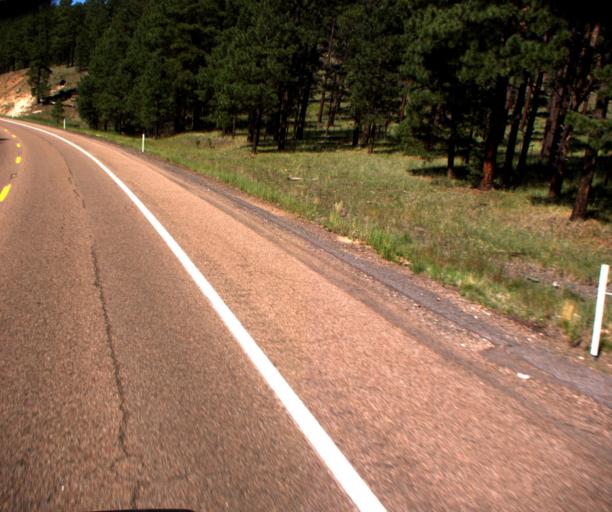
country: US
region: Arizona
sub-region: Apache County
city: Eagar
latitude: 33.8803
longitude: -109.1638
